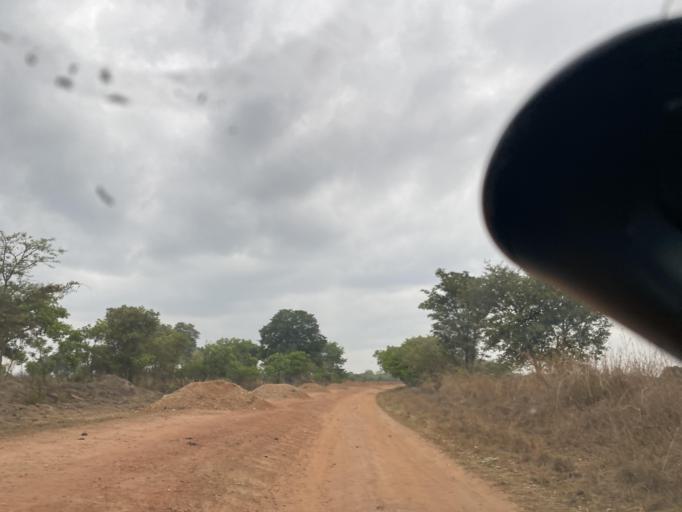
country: ZM
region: Lusaka
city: Chongwe
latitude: -15.2277
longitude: 28.7286
